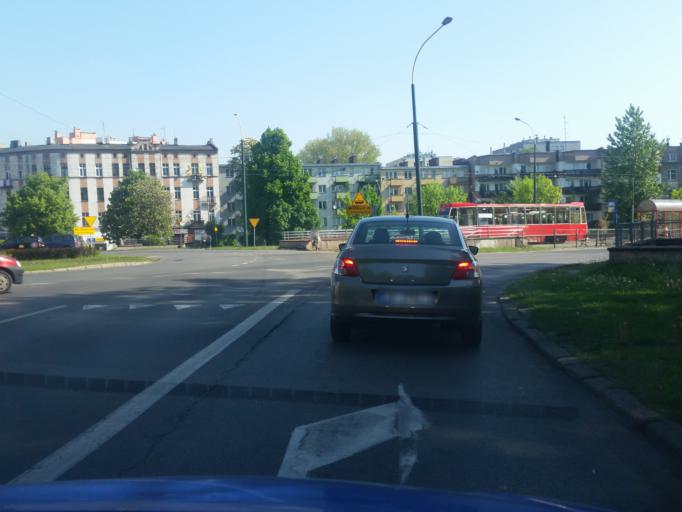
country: PL
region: Silesian Voivodeship
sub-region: Sosnowiec
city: Sosnowiec
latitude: 50.2729
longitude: 19.1350
